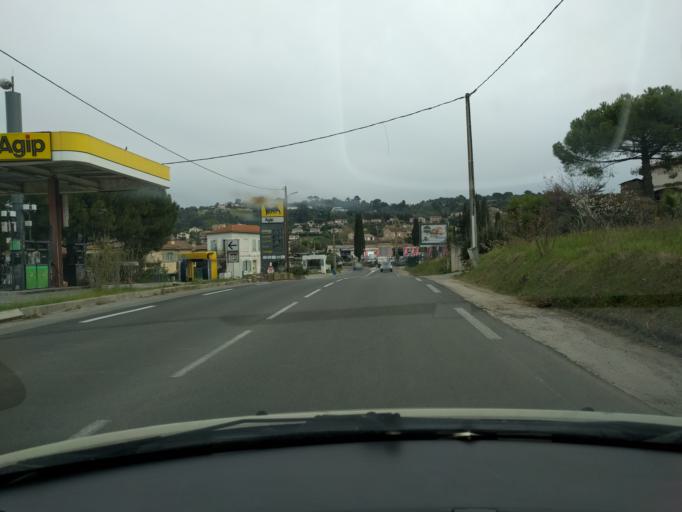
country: FR
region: Provence-Alpes-Cote d'Azur
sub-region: Departement des Alpes-Maritimes
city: La Roquette-sur-Siagne
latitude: 43.5757
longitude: 6.9517
